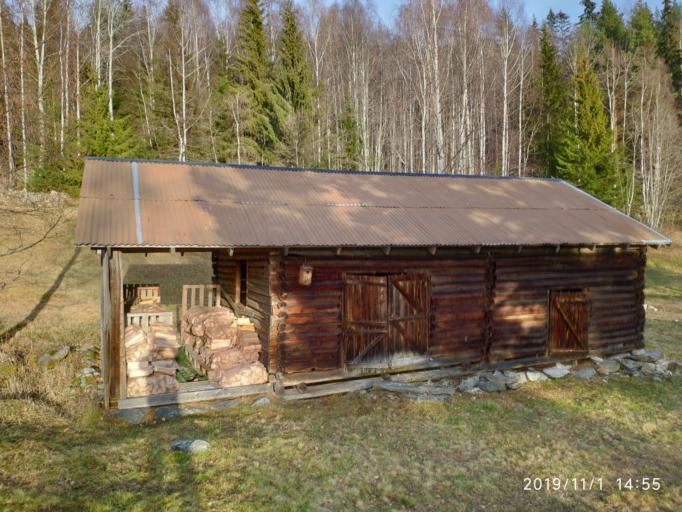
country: NO
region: Buskerud
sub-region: Gol
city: Gol
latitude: 60.7083
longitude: 8.9395
